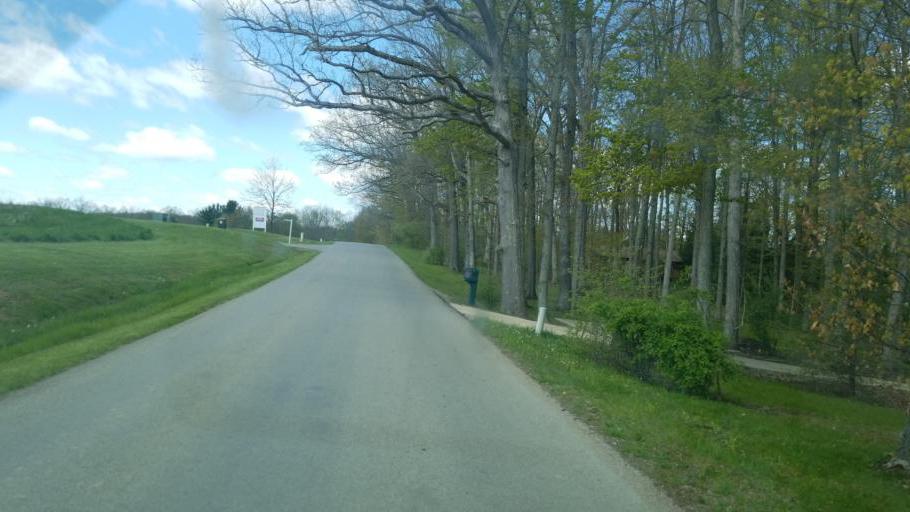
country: US
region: Ohio
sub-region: Knox County
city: Gambier
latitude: 40.4390
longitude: -82.3558
